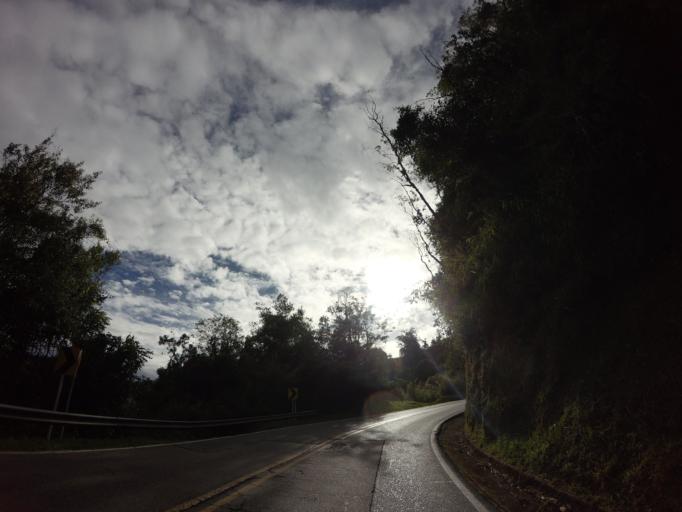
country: CO
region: Tolima
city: Herveo
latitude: 5.1372
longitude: -75.1847
